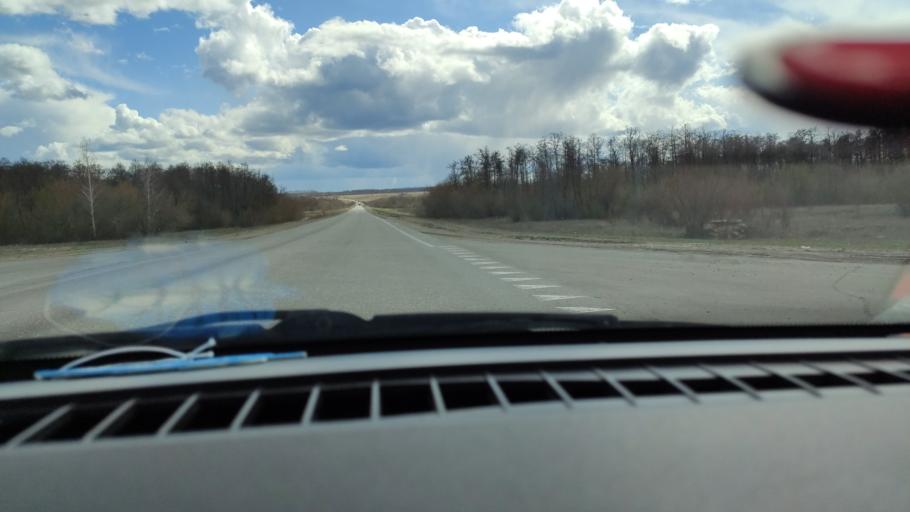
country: RU
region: Samara
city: Varlamovo
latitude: 53.1424
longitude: 48.2848
